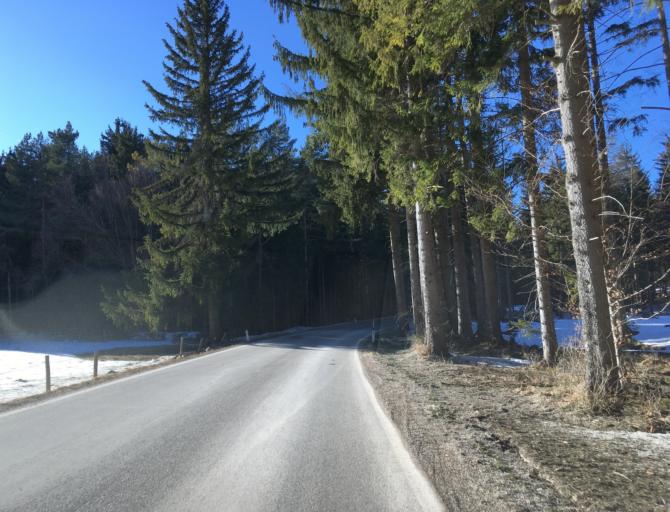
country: AT
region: Lower Austria
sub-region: Politischer Bezirk Wiener Neustadt
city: Waldegg
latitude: 47.8379
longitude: 16.0448
